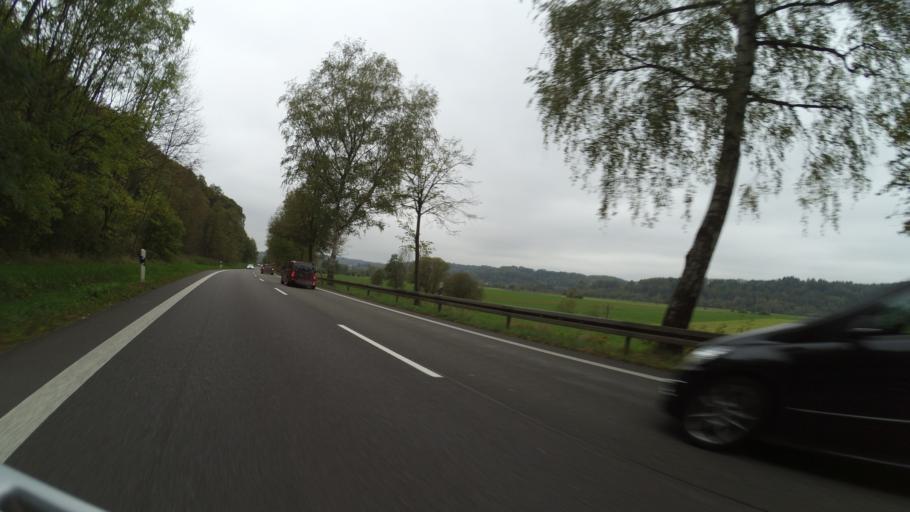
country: DE
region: Saarland
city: Blieskastel
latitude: 49.2517
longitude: 7.2791
